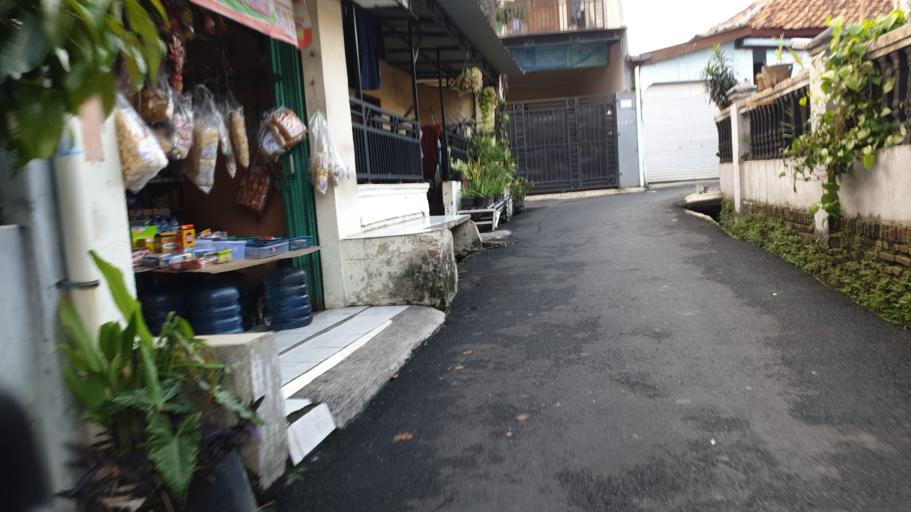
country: ID
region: West Java
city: Depok
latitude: -6.3283
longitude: 106.8317
